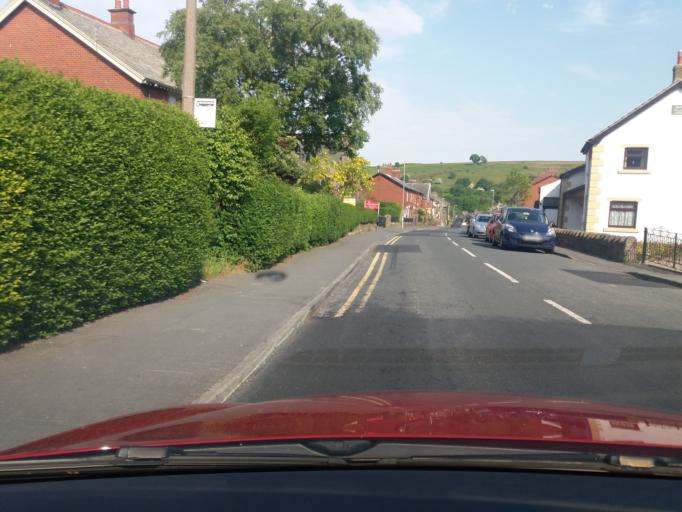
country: GB
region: England
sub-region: Lancashire
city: Chorley
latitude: 53.6888
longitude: -2.5717
